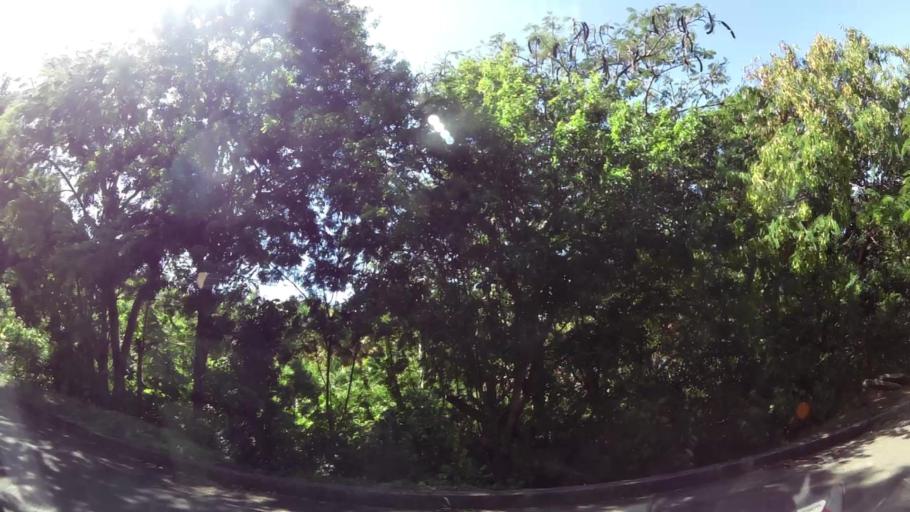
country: LC
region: Vieux-Fort
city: Vieux Fort
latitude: 13.7188
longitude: -60.9499
